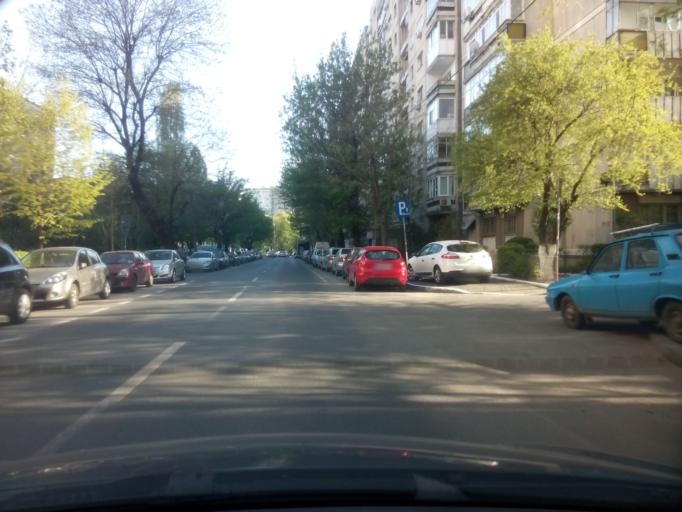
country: RO
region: Ilfov
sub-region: Comuna Fundeni-Dobroesti
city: Fundeni
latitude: 44.4318
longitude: 26.1464
